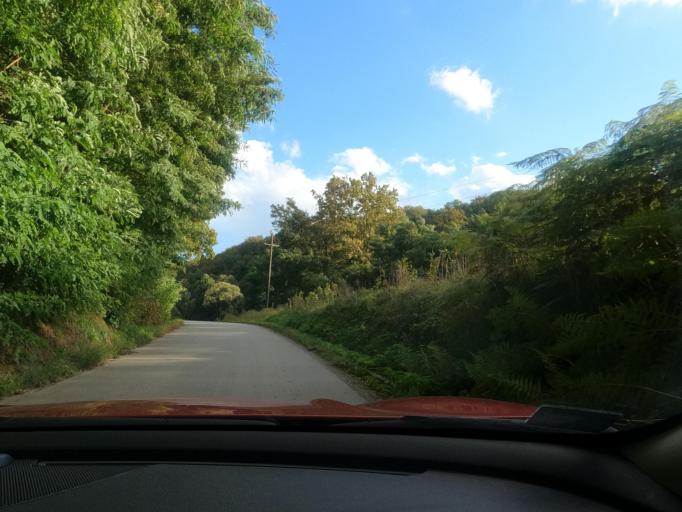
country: HR
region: Sisacko-Moslavacka
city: Petrinja
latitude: 45.3901
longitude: 16.2438
